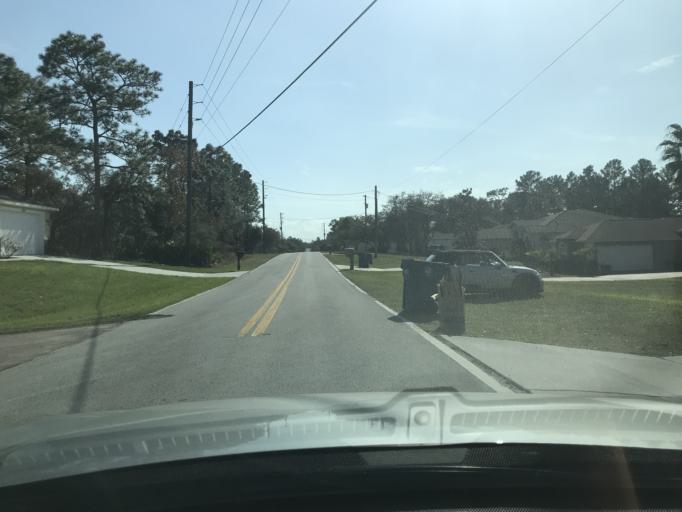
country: US
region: Florida
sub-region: Hernando County
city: North Weeki Wachee
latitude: 28.5450
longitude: -82.5474
